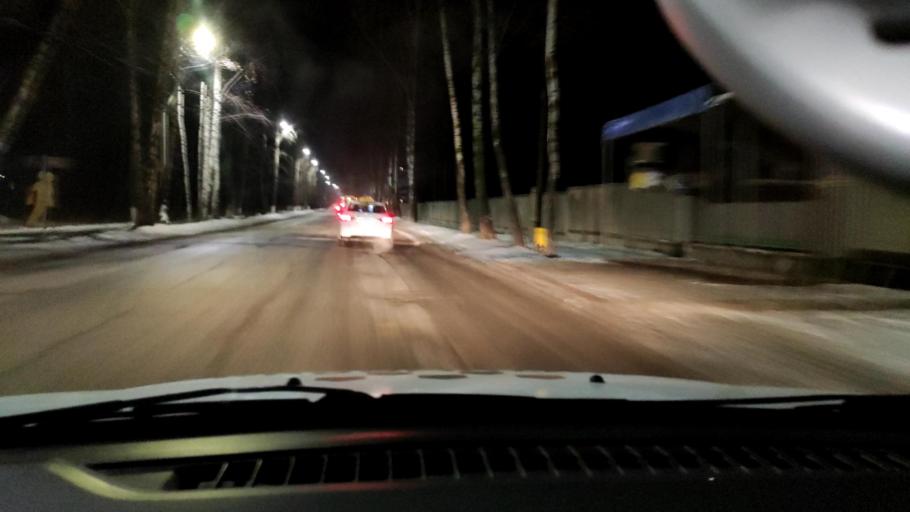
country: RU
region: Perm
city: Kultayevo
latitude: 57.9837
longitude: 55.9205
